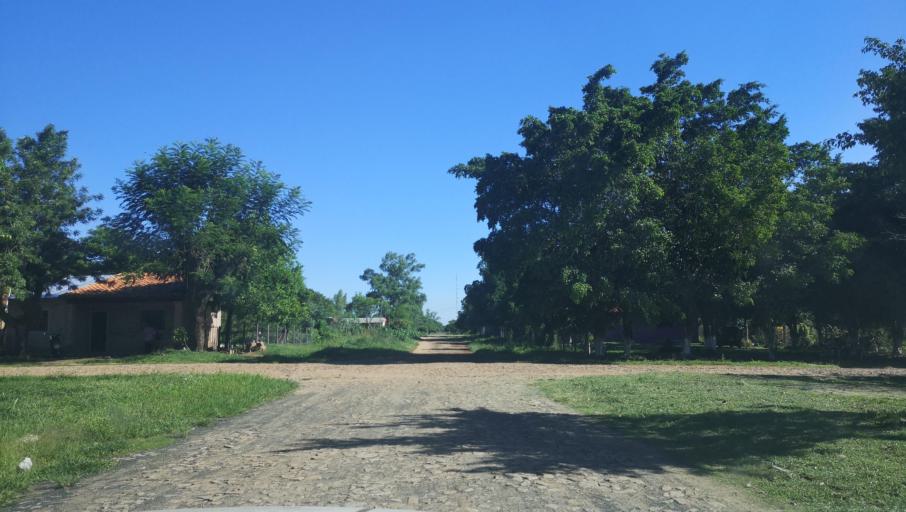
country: PY
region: Caaguazu
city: Carayao
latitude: -25.1983
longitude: -56.3990
